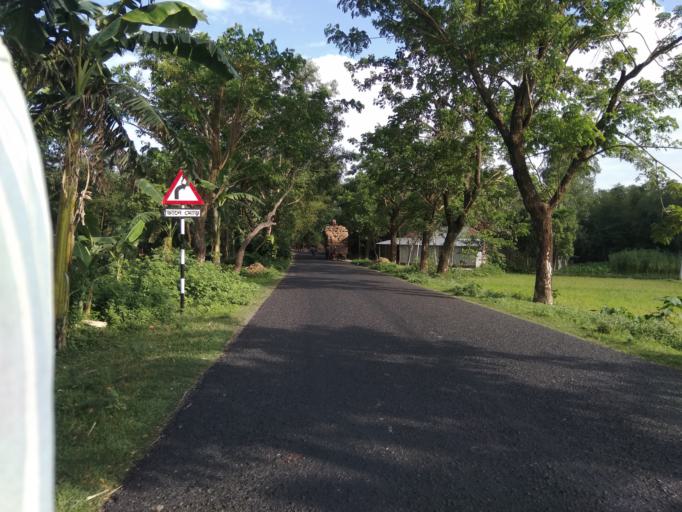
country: BD
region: Rangpur Division
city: Rangpur
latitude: 25.8415
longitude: 89.1133
